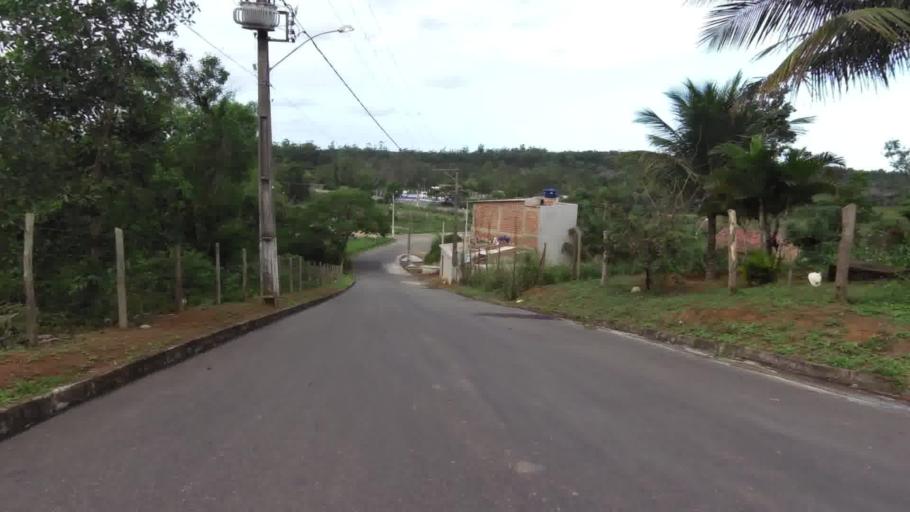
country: BR
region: Espirito Santo
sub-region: Piuma
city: Piuma
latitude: -20.7968
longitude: -40.6416
